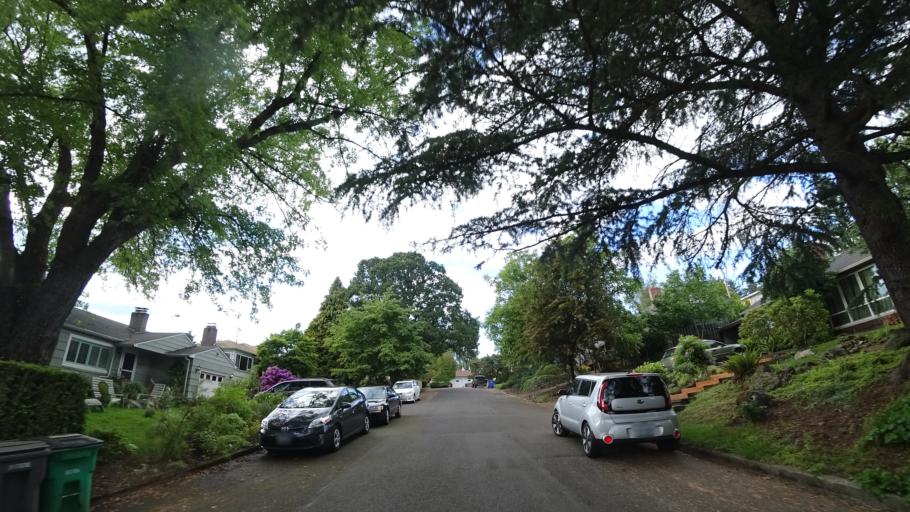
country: US
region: Oregon
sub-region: Washington County
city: Raleigh Hills
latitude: 45.4805
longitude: -122.7242
